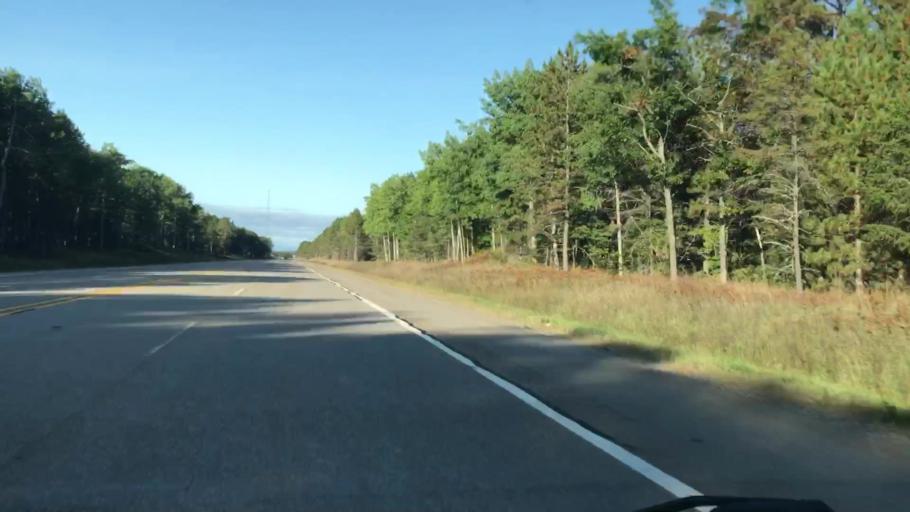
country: US
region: Michigan
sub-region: Chippewa County
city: Sault Ste. Marie
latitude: 46.3630
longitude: -84.7716
